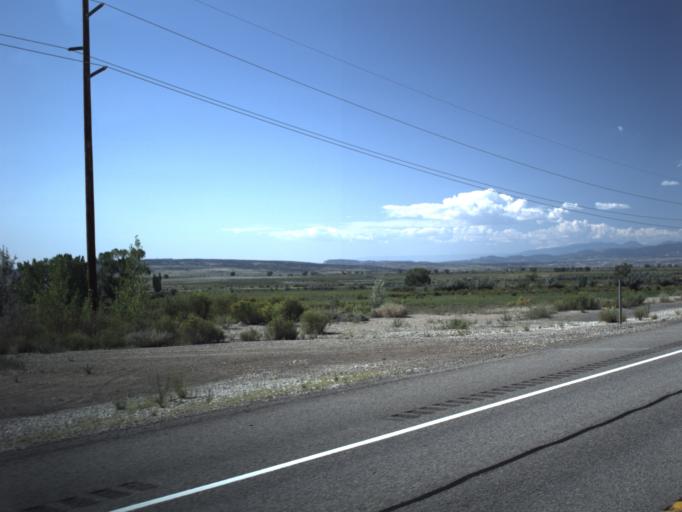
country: US
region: Utah
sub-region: Emery County
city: Ferron
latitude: 38.9339
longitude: -111.2298
